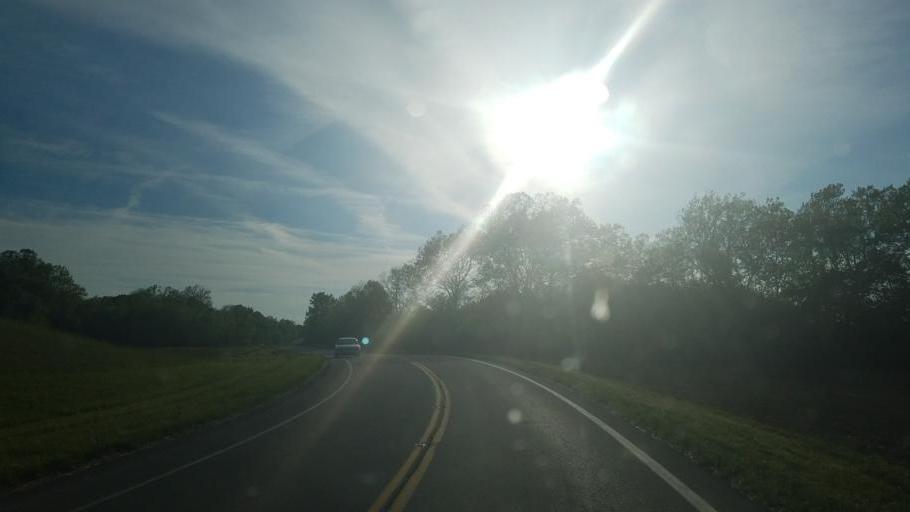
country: US
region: Ohio
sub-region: Ross County
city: Frankfort
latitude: 39.4282
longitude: -83.2305
